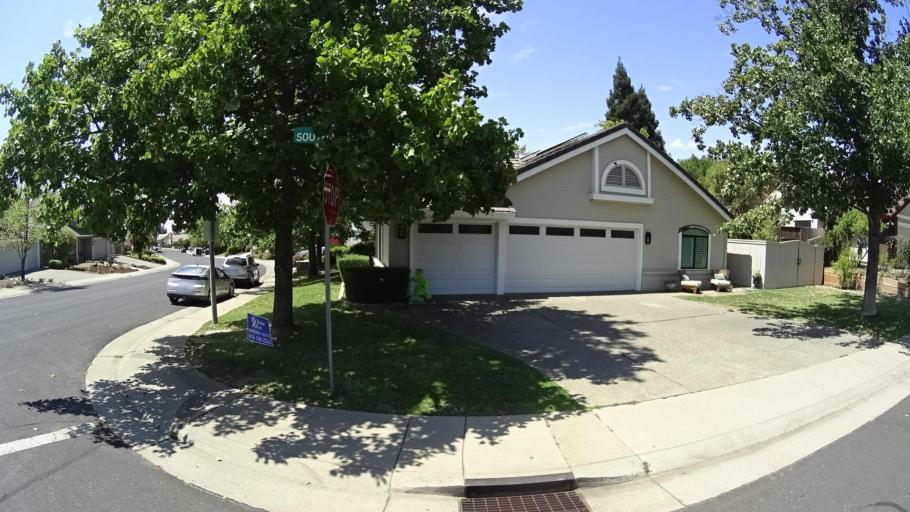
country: US
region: California
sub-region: Placer County
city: Rocklin
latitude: 38.8093
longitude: -121.2488
